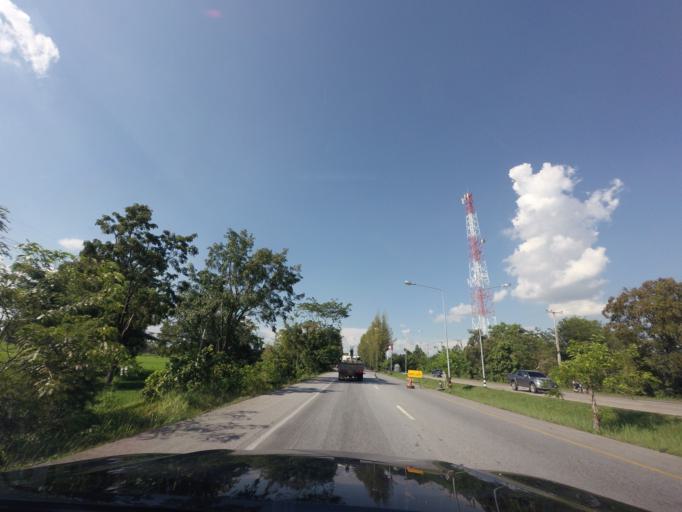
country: TH
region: Nakhon Ratchasima
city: Sida
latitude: 15.5363
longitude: 102.5452
